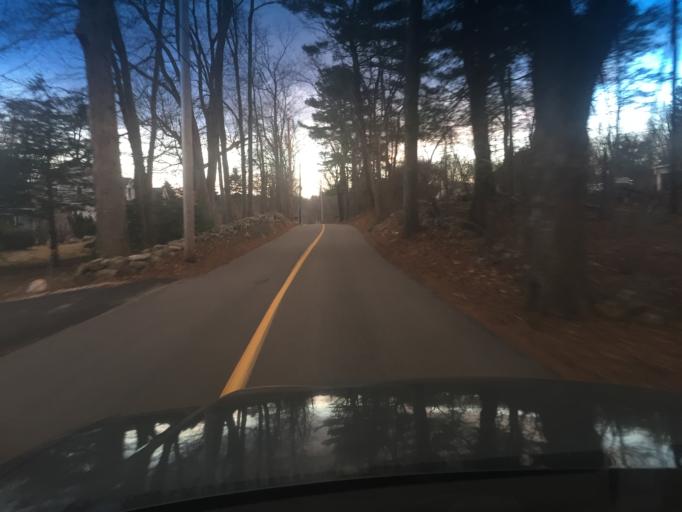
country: US
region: Massachusetts
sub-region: Middlesex County
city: Holliston
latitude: 42.1575
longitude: -71.4388
